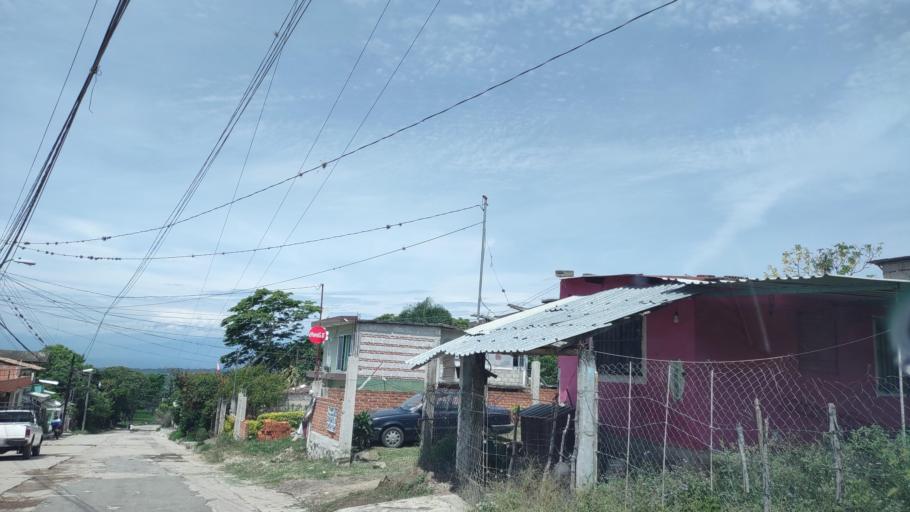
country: MX
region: Veracruz
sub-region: Emiliano Zapata
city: Jacarandas
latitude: 19.4683
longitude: -96.8314
